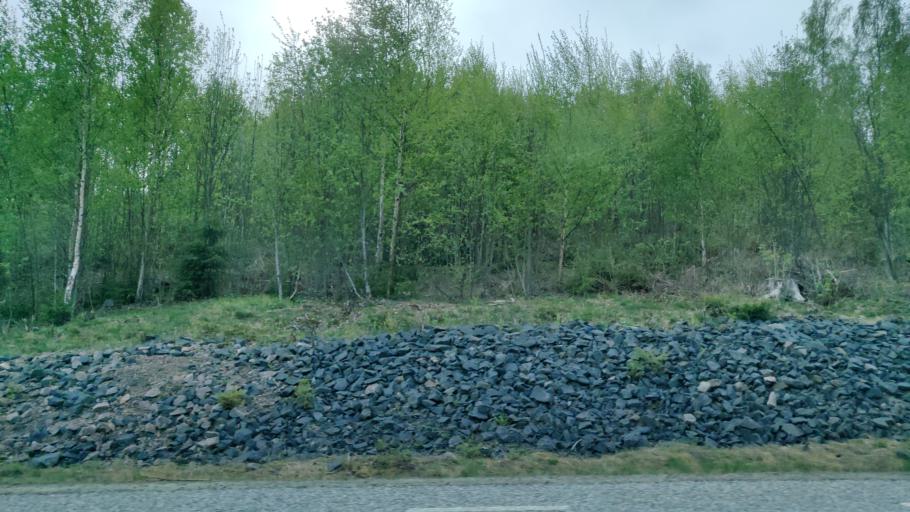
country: SE
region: Vaermland
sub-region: Munkfors Kommun
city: Munkfors
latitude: 59.7548
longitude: 13.4431
